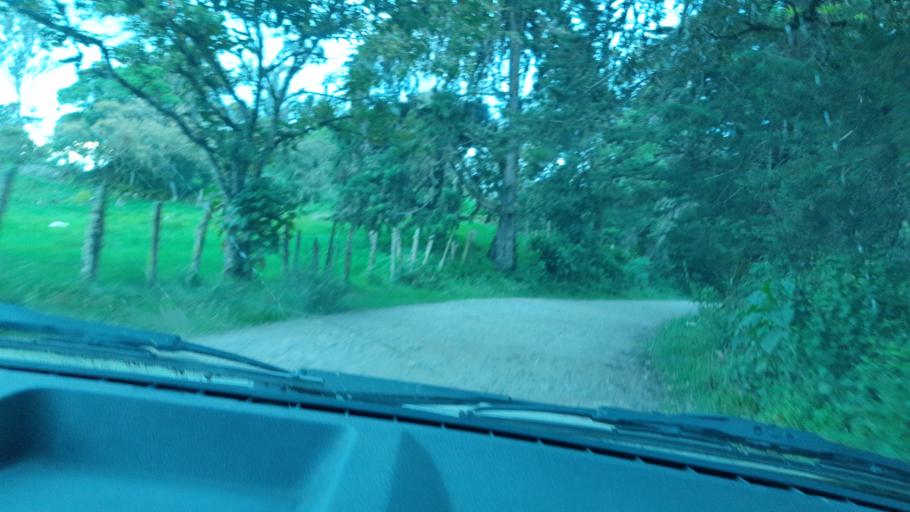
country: CO
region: Boyaca
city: Garagoa
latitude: 5.0897
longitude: -73.3339
